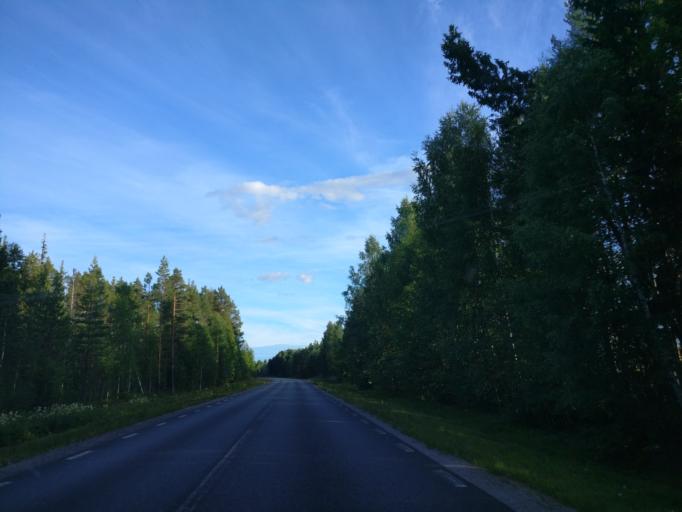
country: SE
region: Jaemtland
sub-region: Braecke Kommun
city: Braecke
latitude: 62.4111
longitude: 15.0156
